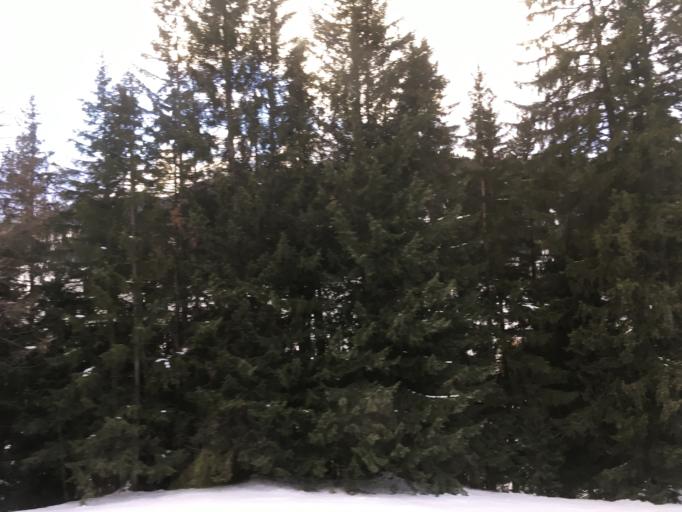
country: CH
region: Grisons
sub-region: Albula District
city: Tiefencastel
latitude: 46.7149
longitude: 9.5587
